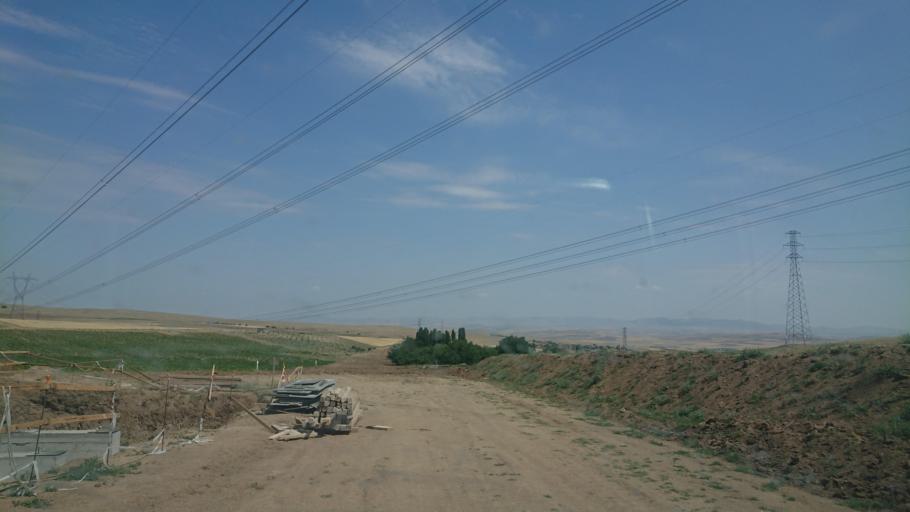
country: TR
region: Aksaray
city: Agacoren
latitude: 38.9017
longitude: 33.9241
